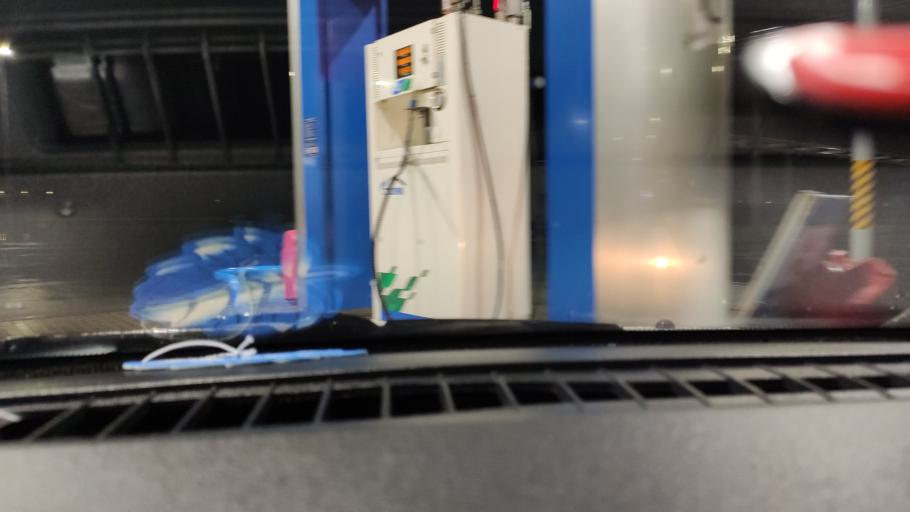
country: RU
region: Udmurtiya
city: Votkinsk
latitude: 57.0361
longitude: 54.0256
